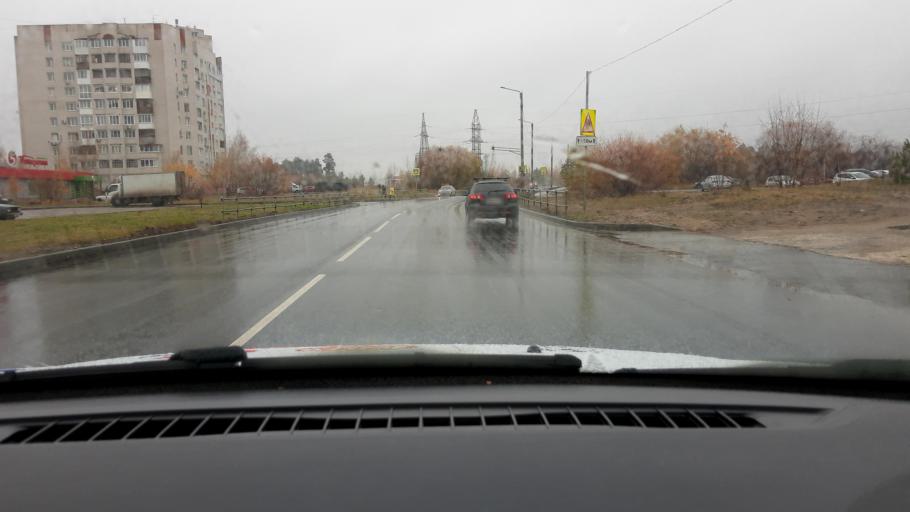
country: RU
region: Nizjnij Novgorod
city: Dzerzhinsk
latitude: 56.2340
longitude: 43.4087
